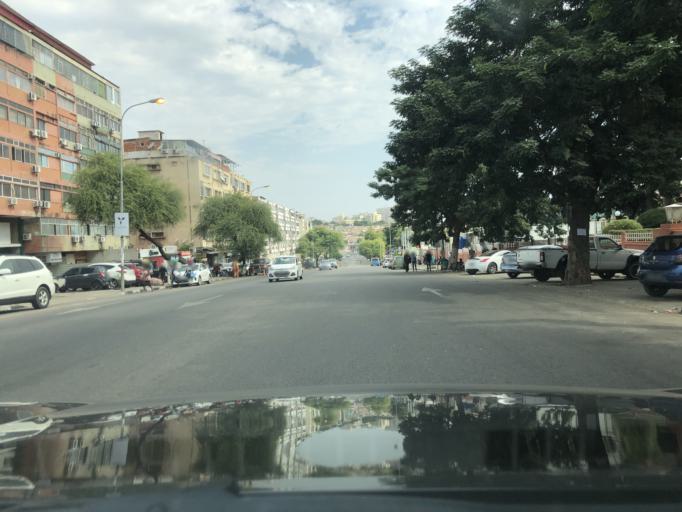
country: AO
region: Luanda
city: Luanda
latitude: -8.8257
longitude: 13.2277
